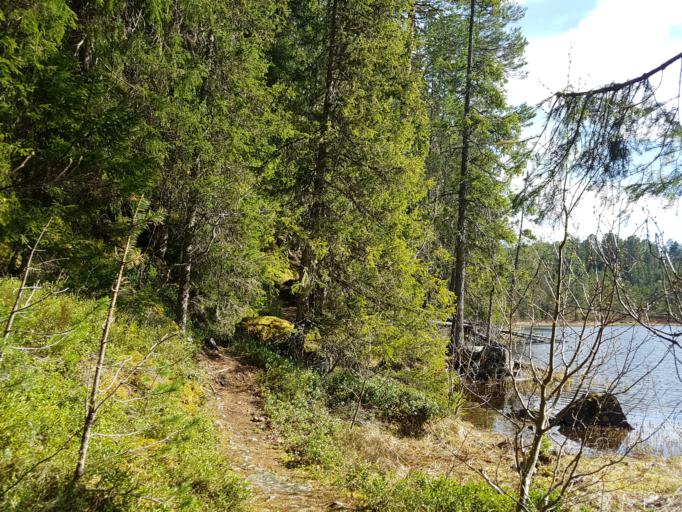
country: NO
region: Sor-Trondelag
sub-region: Trondheim
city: Trondheim
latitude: 63.4397
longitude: 10.2919
